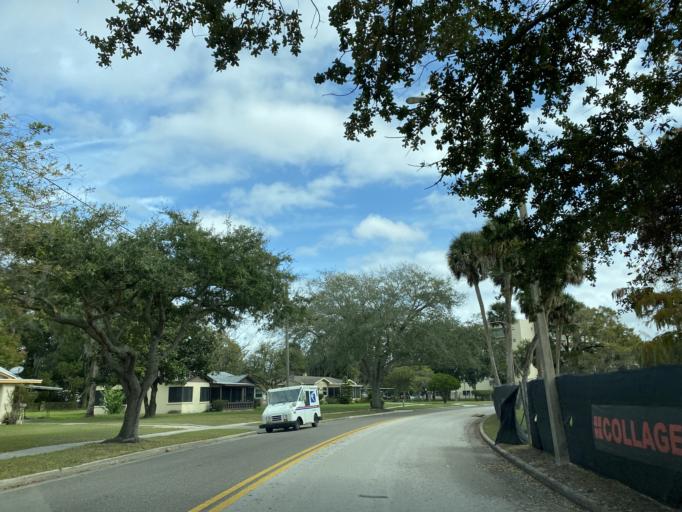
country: US
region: Florida
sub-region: Orange County
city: Orlando
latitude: 28.5427
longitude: -81.4040
